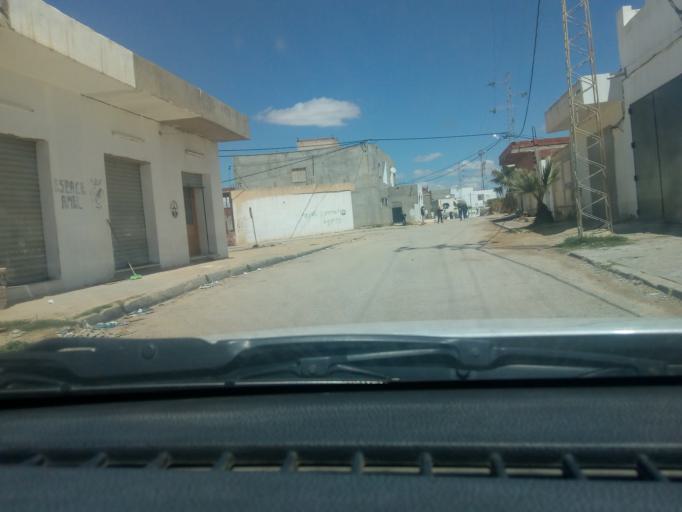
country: TN
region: Safaqis
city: Sfax
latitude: 34.7410
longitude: 10.5238
